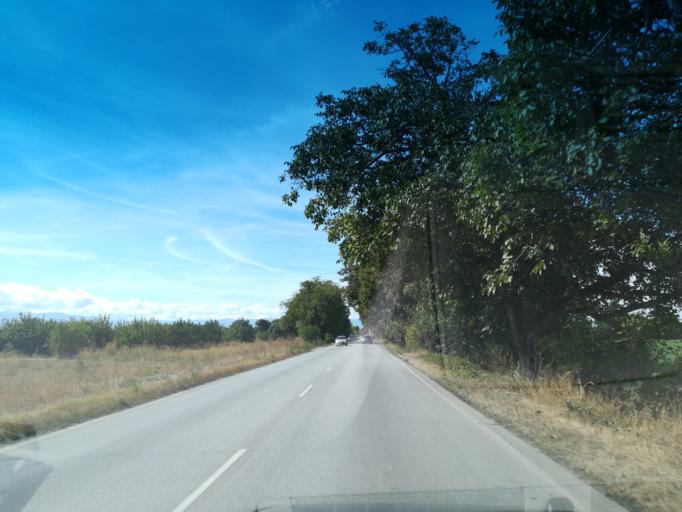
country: BG
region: Plovdiv
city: Stamboliyski
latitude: 42.1344
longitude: 24.6176
